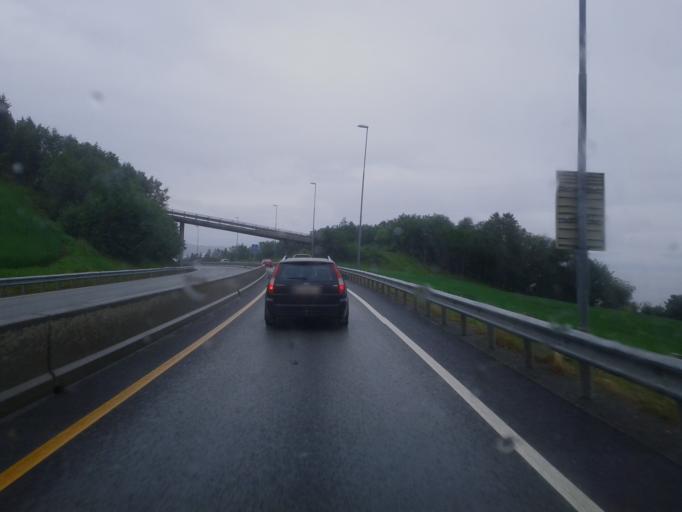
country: NO
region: Sor-Trondelag
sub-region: Malvik
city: Malvik
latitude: 63.4249
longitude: 10.5742
